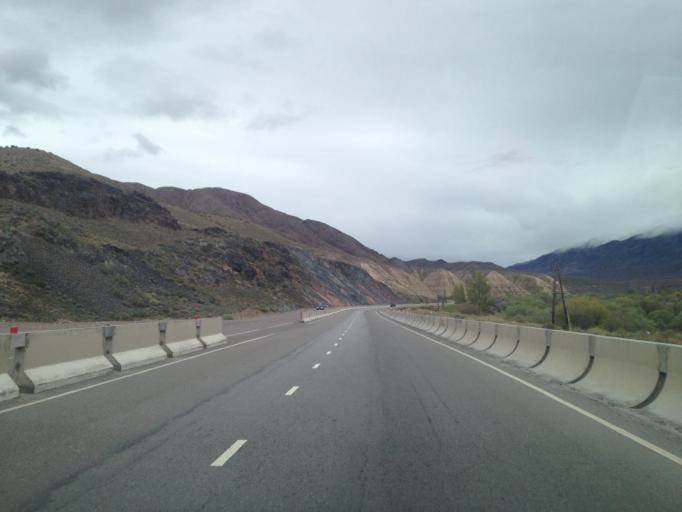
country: KG
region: Naryn
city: Kochkor
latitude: 42.4960
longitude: 75.8451
